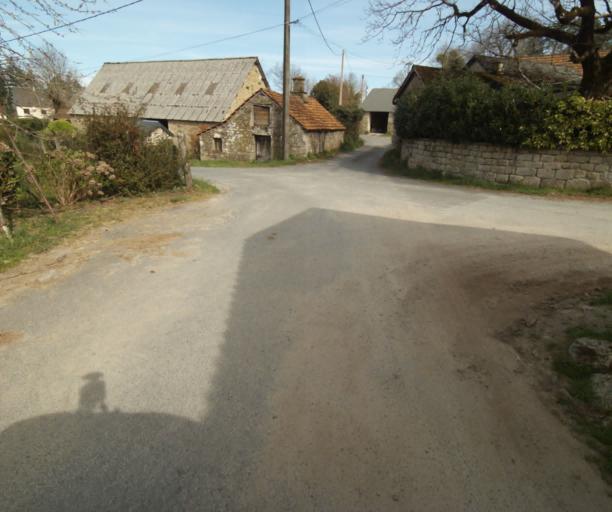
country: FR
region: Limousin
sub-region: Departement de la Correze
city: Correze
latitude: 45.4115
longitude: 1.8287
